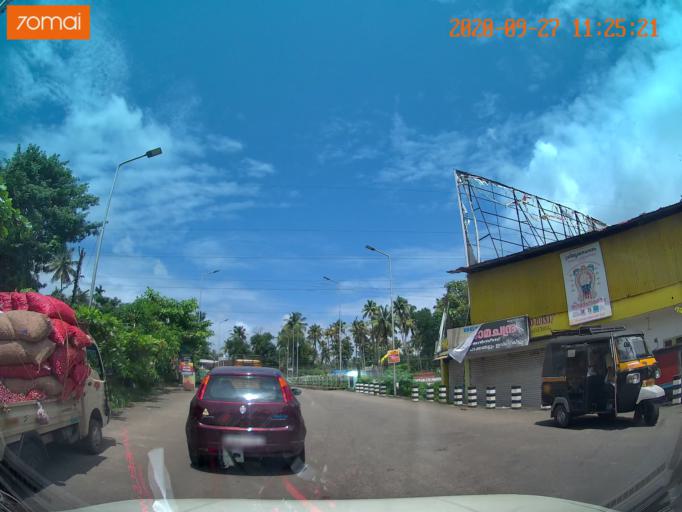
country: IN
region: Kerala
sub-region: Thrissur District
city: Thanniyam
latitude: 10.4137
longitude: 76.1580
